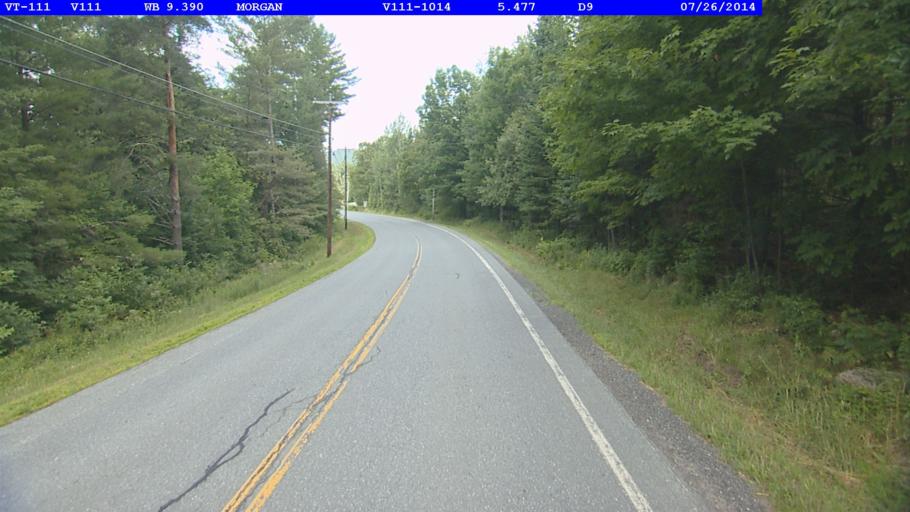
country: US
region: Vermont
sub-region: Orleans County
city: Newport
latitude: 44.9019
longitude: -71.9756
